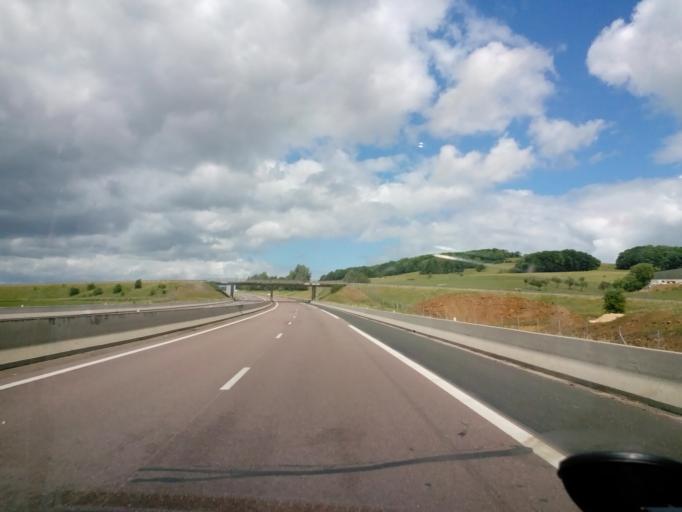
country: FR
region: Lorraine
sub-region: Departement des Vosges
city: Chatenois
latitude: 48.3283
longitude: 5.8564
